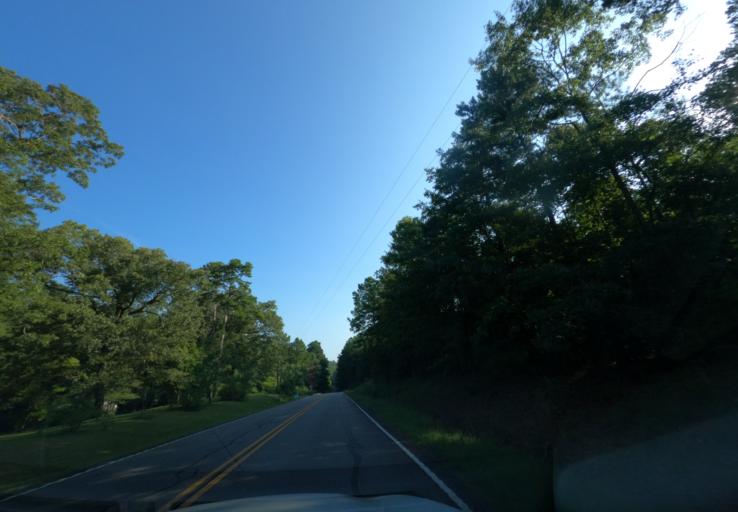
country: US
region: South Carolina
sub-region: Edgefield County
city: Murphys Estates
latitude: 33.5897
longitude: -81.9792
